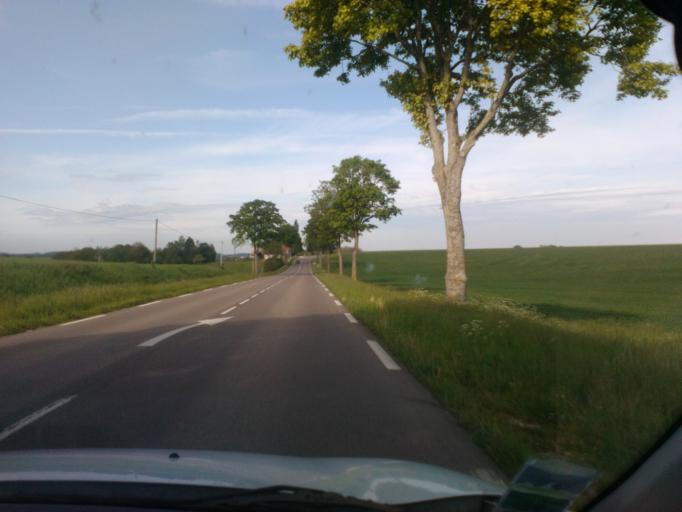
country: FR
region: Champagne-Ardenne
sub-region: Departement de l'Aube
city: Vendeuvre-sur-Barse
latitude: 48.2370
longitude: 4.5225
